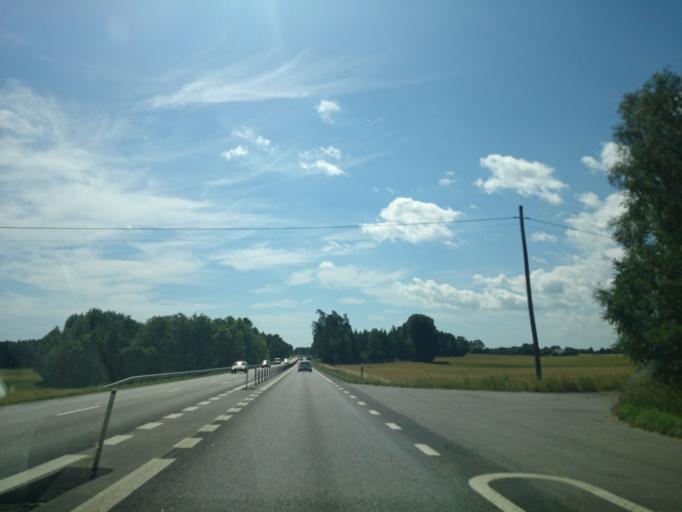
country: SE
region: Kalmar
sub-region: Kalmar Kommun
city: Lindsdal
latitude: 56.8250
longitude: 16.3682
